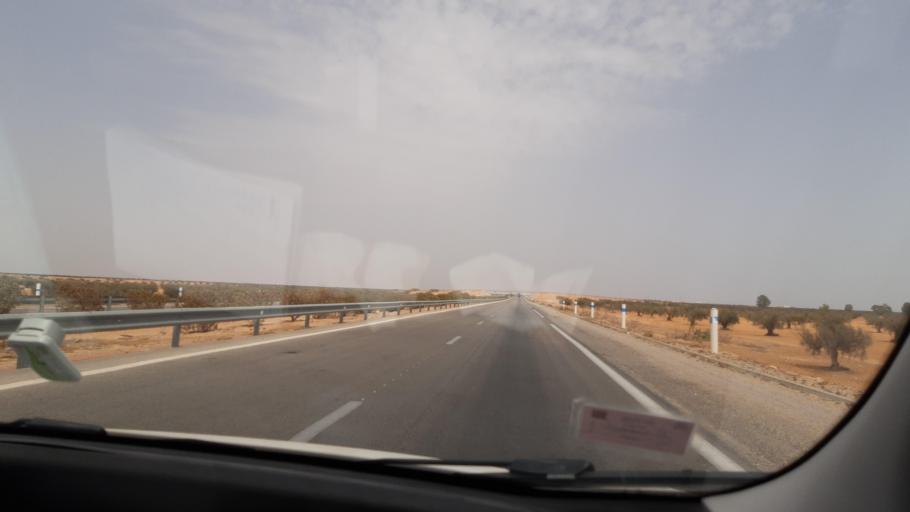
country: TN
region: Safaqis
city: Bi'r `Ali Bin Khalifah
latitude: 34.5844
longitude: 10.4050
